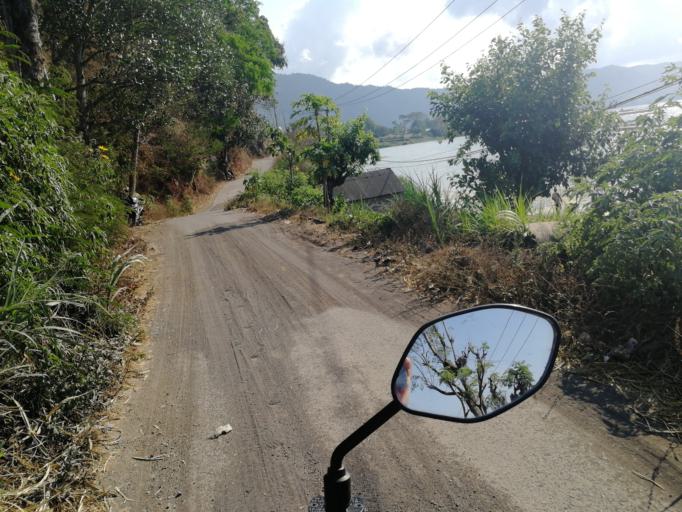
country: ID
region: Bali
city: Banjar Trunyan
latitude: -8.2671
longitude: 115.4196
